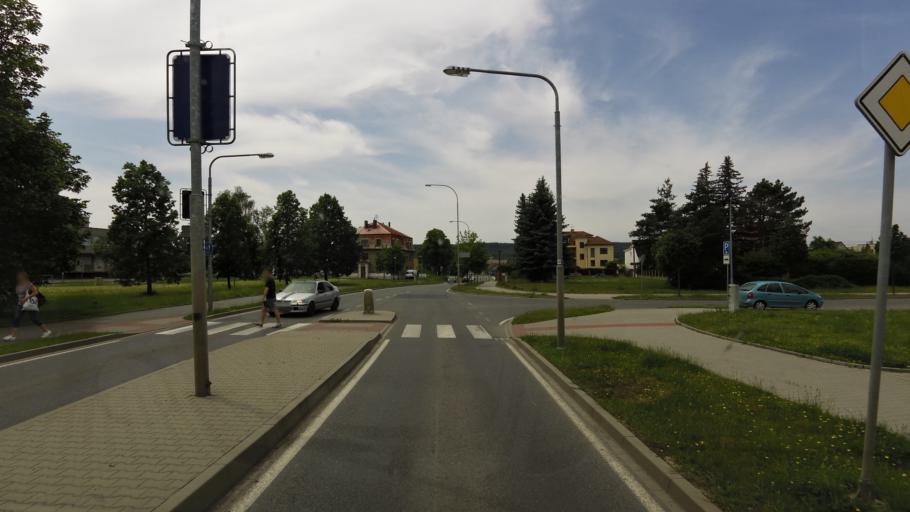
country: CZ
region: Plzensky
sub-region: Okres Rokycany
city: Rokycany
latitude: 49.7340
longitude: 13.5915
